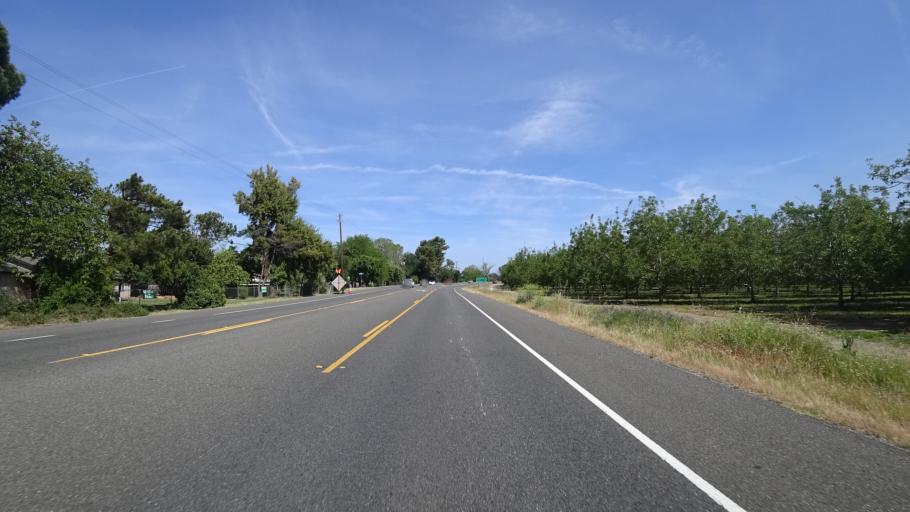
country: US
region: California
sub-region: Tehama County
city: Red Bluff
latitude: 40.1850
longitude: -122.1787
